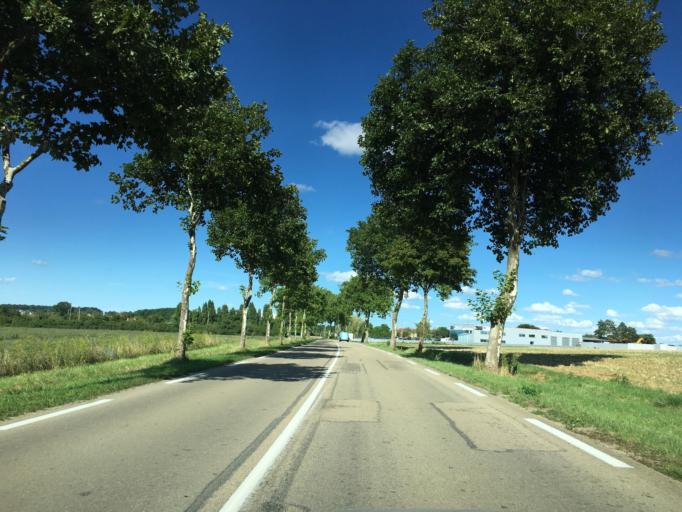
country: FR
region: Bourgogne
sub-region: Departement de l'Yonne
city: Saint-Georges-sur-Baulche
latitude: 47.7852
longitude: 3.5284
